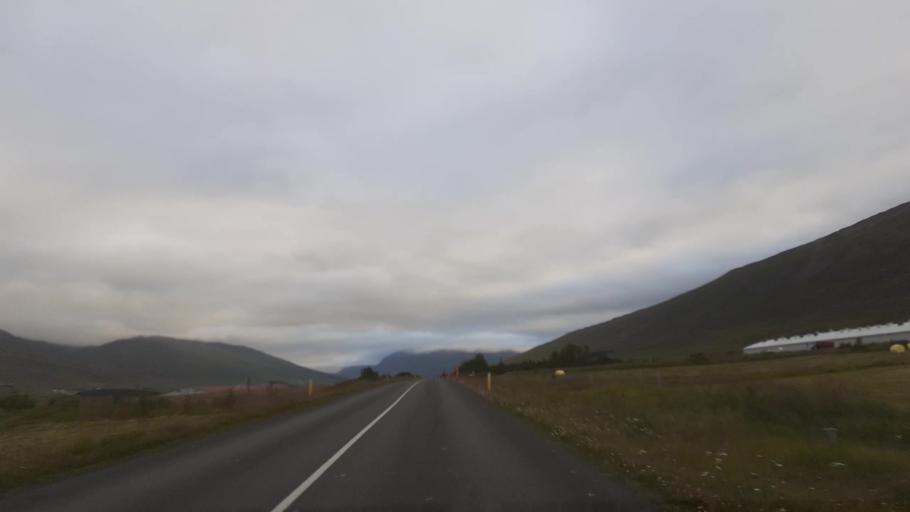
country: IS
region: Northeast
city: Dalvik
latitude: 65.9539
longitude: -18.5518
